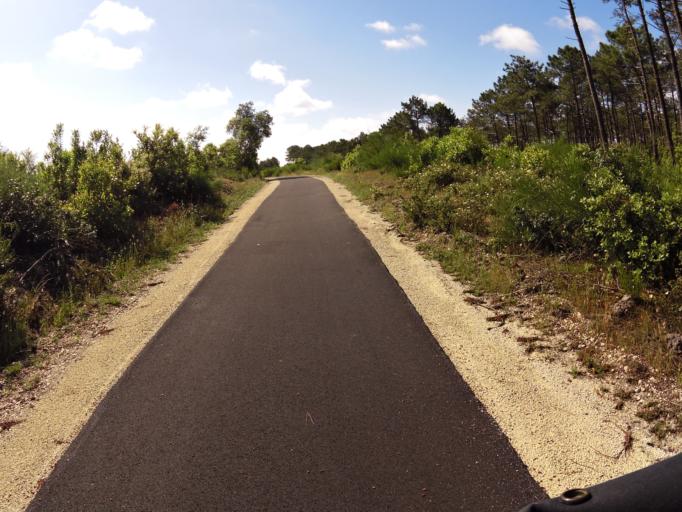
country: FR
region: Aquitaine
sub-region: Departement de la Gironde
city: Lacanau
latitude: 45.0333
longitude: -1.1800
